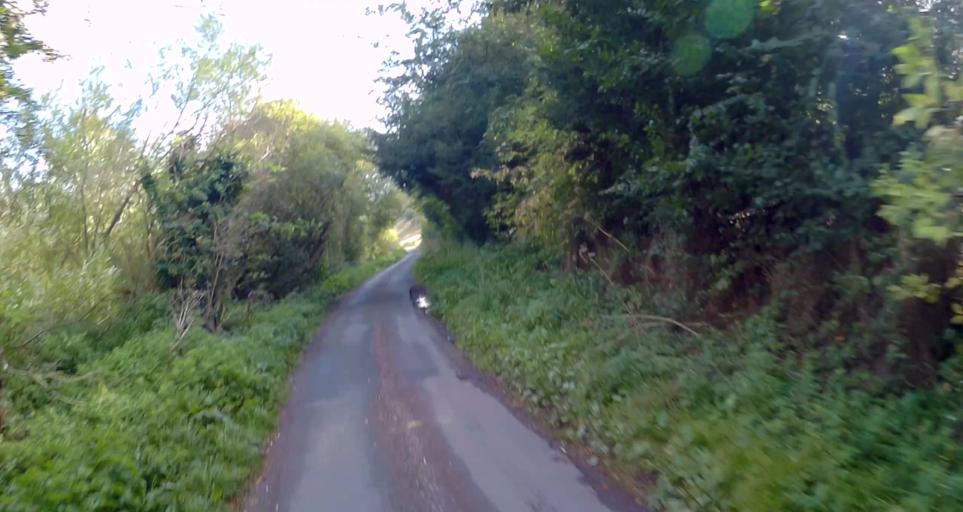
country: GB
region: England
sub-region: Hampshire
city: Kings Worthy
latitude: 51.0903
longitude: -1.2224
